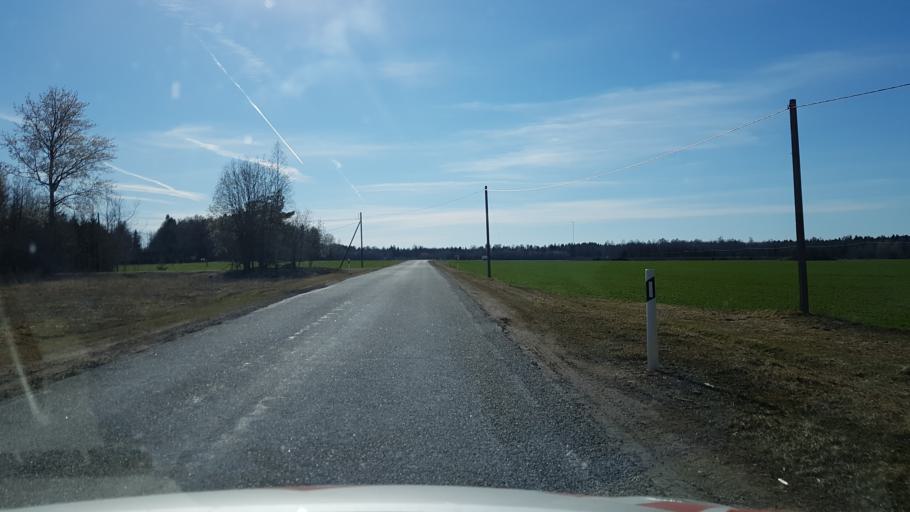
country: EE
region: Ida-Virumaa
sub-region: Aseri vald
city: Aseri
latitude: 59.2306
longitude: 26.7302
